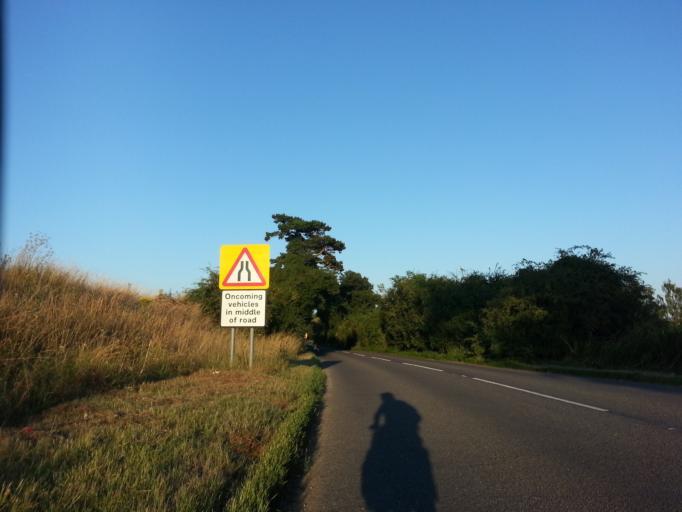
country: GB
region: England
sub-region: Suffolk
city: Kesgrave
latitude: 52.1040
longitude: 1.2667
